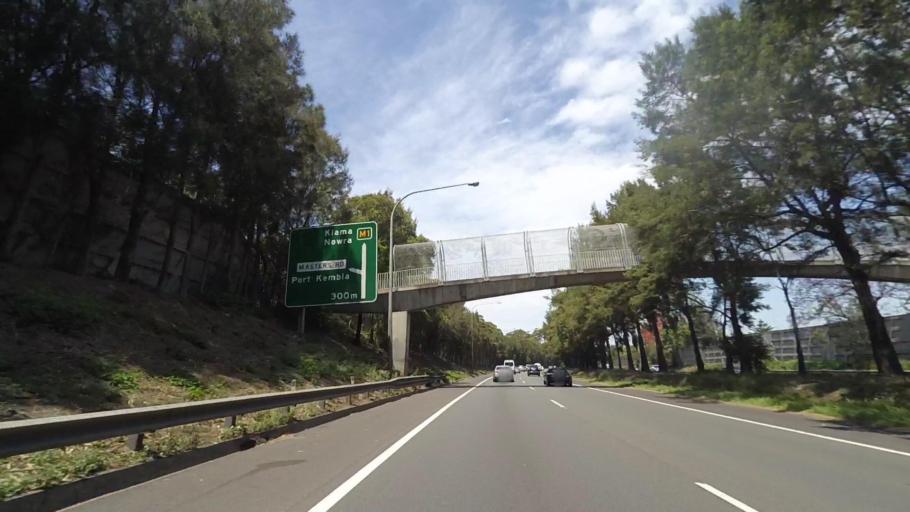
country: AU
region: New South Wales
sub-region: Wollongong
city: Mangerton
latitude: -34.4348
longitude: 150.8685
